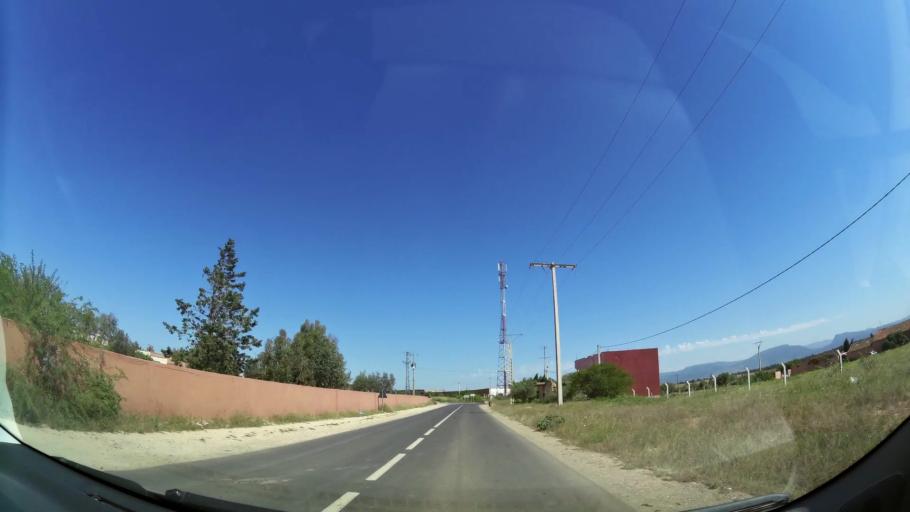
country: MA
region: Oriental
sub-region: Berkane-Taourirt
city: Madagh
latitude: 35.0125
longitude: -2.3983
